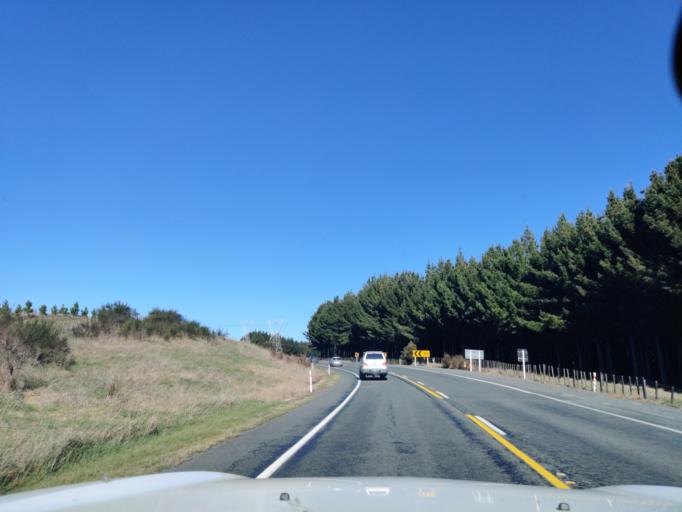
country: NZ
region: Waikato
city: Turangi
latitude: -39.0844
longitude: 175.8072
